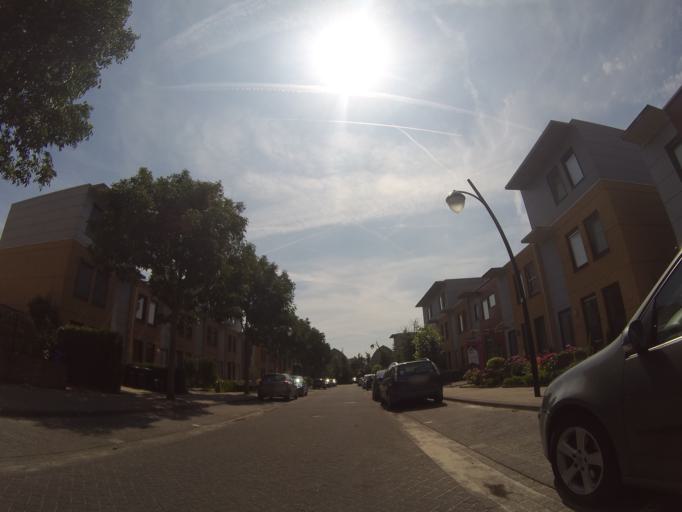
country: NL
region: Utrecht
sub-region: Gemeente Amersfoort
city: Hoogland
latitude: 52.1980
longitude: 5.4233
